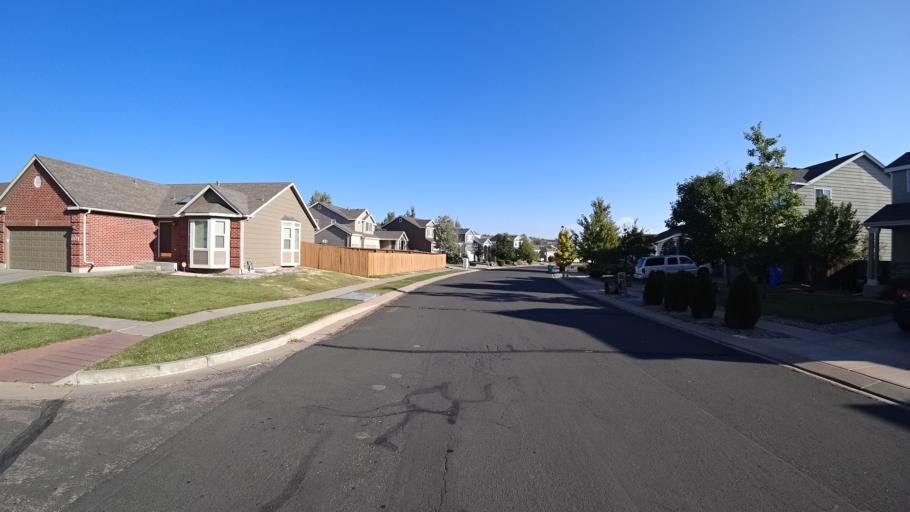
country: US
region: Colorado
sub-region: El Paso County
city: Cimarron Hills
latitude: 38.8918
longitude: -104.6947
